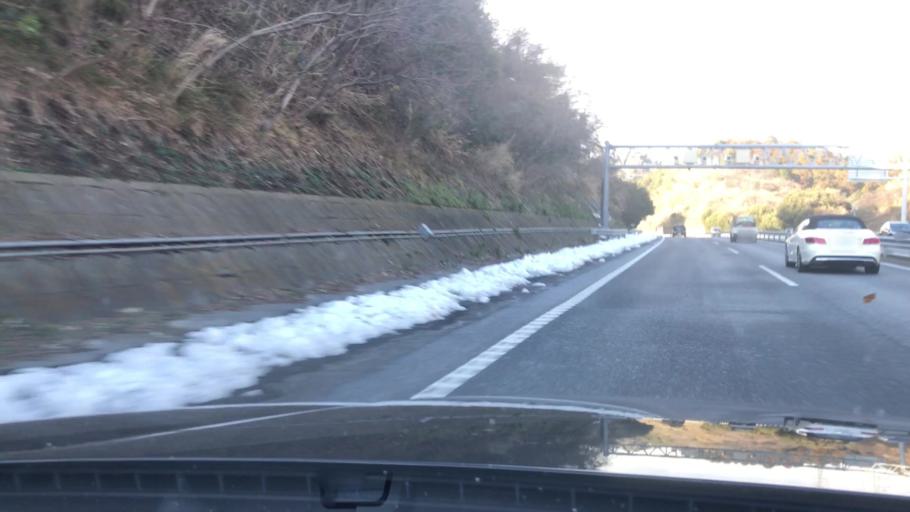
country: JP
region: Kanagawa
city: Zushi
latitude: 35.2975
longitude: 139.6171
